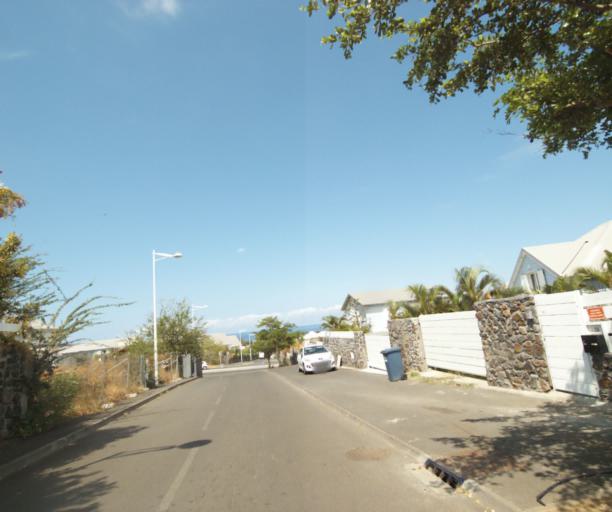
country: RE
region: Reunion
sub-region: Reunion
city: Trois-Bassins
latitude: -21.0902
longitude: 55.2414
